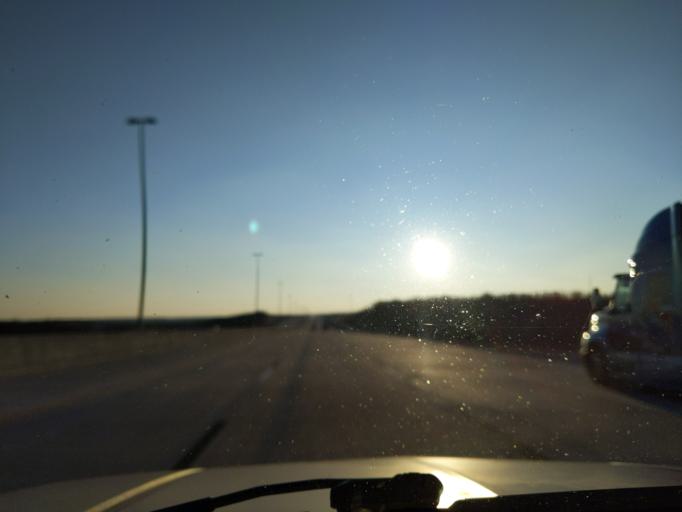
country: US
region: Oklahoma
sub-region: Creek County
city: Kellyville
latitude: 35.9541
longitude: -96.2401
